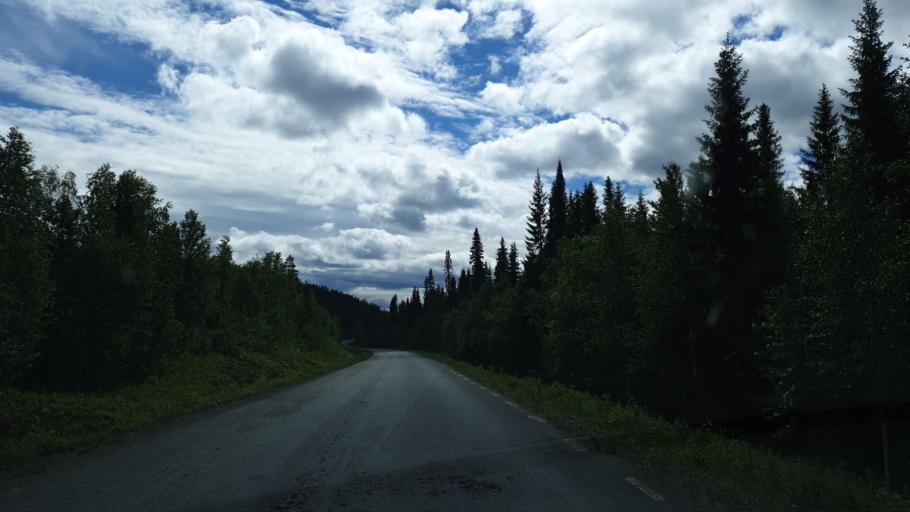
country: SE
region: Vaesterbotten
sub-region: Vilhelmina Kommun
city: Sjoberg
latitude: 64.9653
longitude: 15.8596
